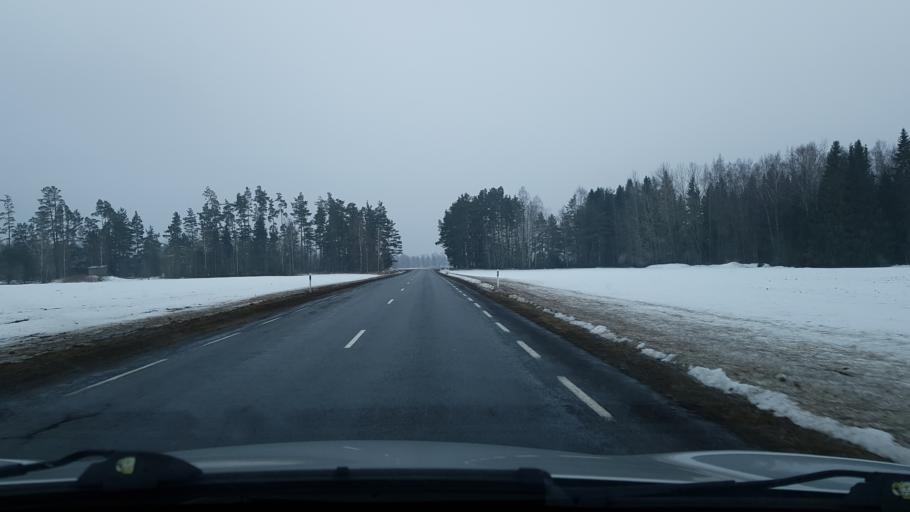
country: EE
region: Valgamaa
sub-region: Torva linn
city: Torva
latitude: 58.2014
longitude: 25.9512
